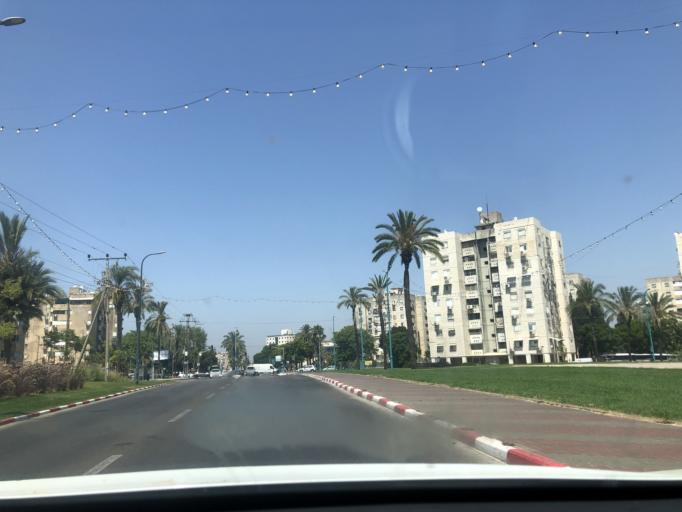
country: IL
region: Central District
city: Lod
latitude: 31.9423
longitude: 34.8886
